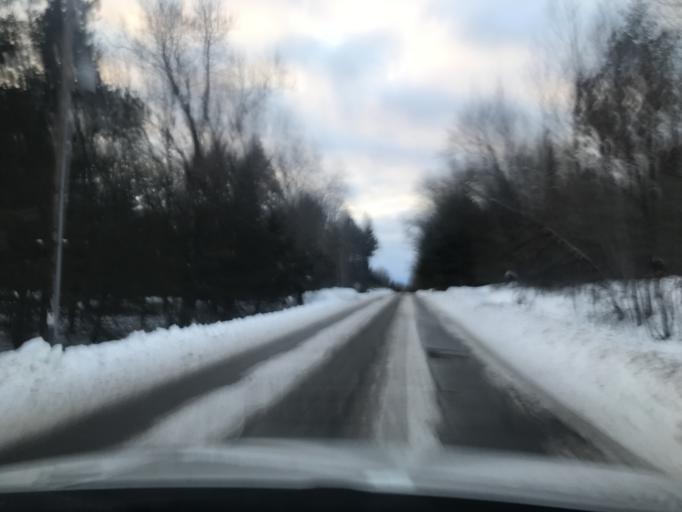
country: US
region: Wisconsin
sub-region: Marinette County
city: Peshtigo
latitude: 45.1643
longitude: -87.7292
